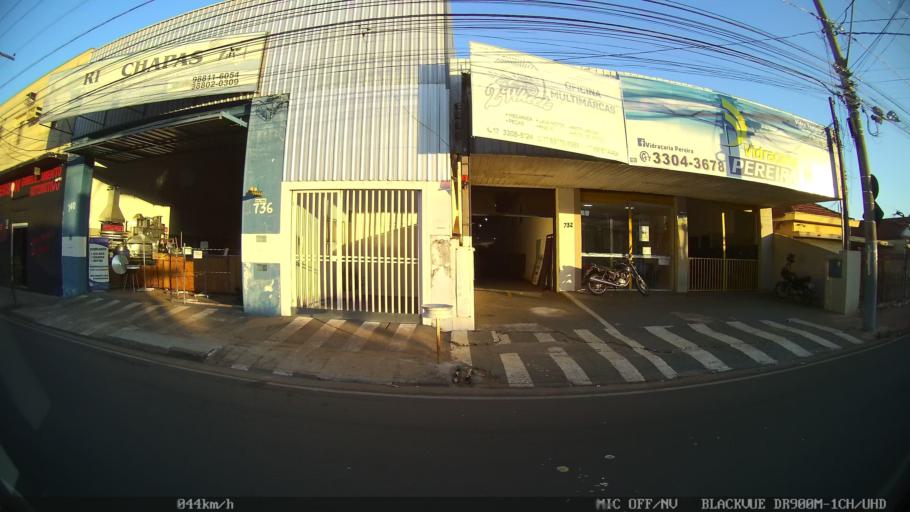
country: BR
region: Sao Paulo
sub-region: Sao Jose Do Rio Preto
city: Sao Jose do Rio Preto
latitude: -20.8047
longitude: -49.3675
